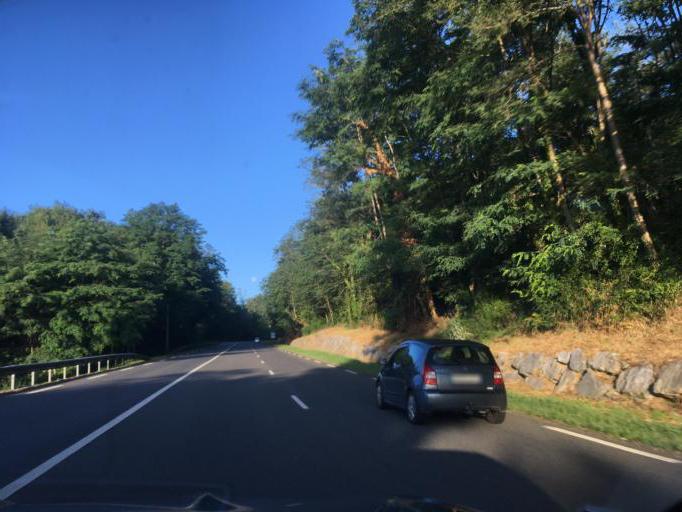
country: FR
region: Midi-Pyrenees
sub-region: Departement des Hautes-Pyrenees
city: Ibos
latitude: 43.2423
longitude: -0.0195
